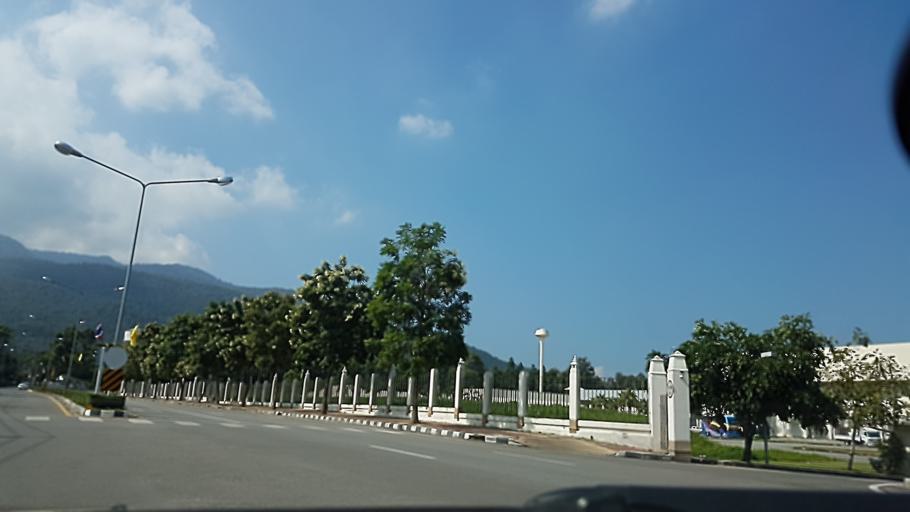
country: TH
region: Chiang Mai
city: Chiang Mai
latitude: 18.8251
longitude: 98.9592
